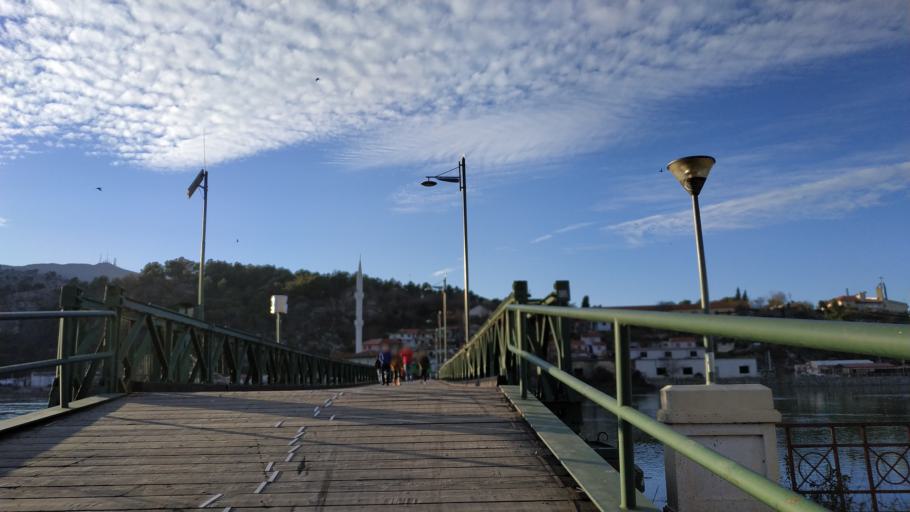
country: AL
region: Shkoder
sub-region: Rrethi i Shkodres
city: Shkoder
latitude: 42.0506
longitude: 19.4922
